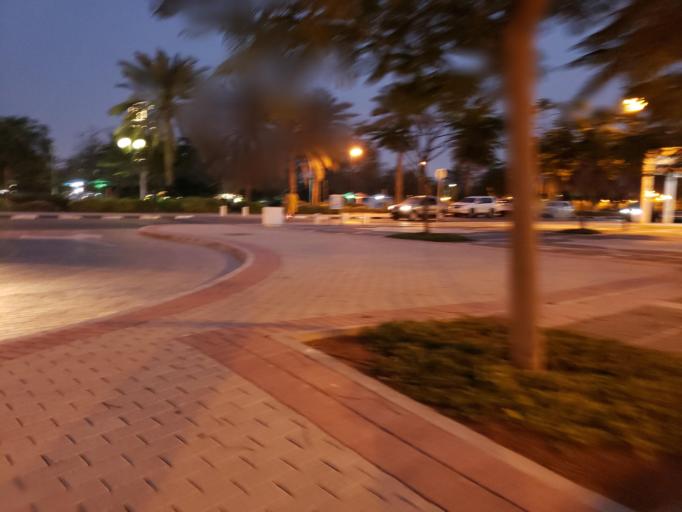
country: AE
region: Ash Shariqah
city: Sharjah
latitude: 25.3241
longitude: 55.3516
